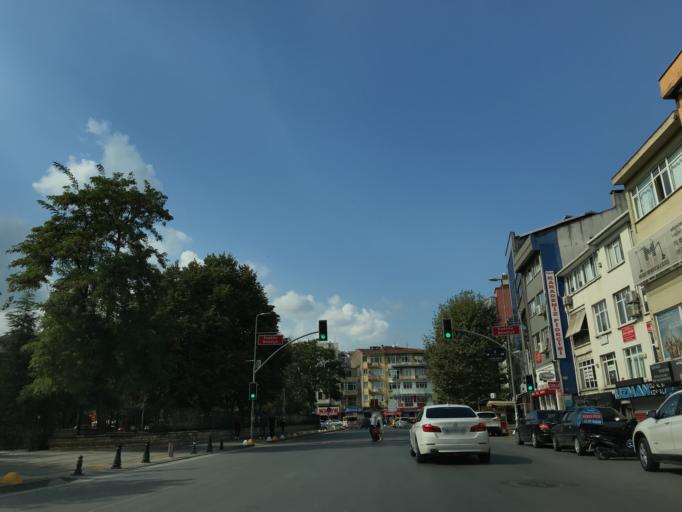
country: TR
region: Istanbul
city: UEskuedar
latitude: 40.9934
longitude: 29.0383
